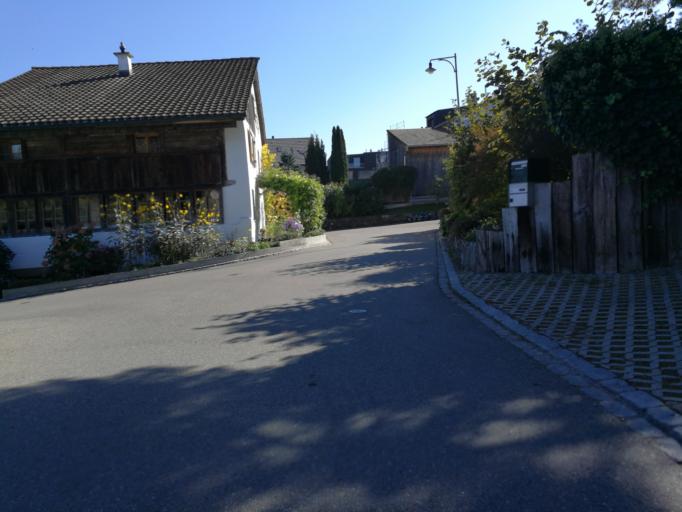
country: CH
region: Zurich
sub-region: Bezirk Uster
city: Aesch
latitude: 47.3380
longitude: 8.6690
